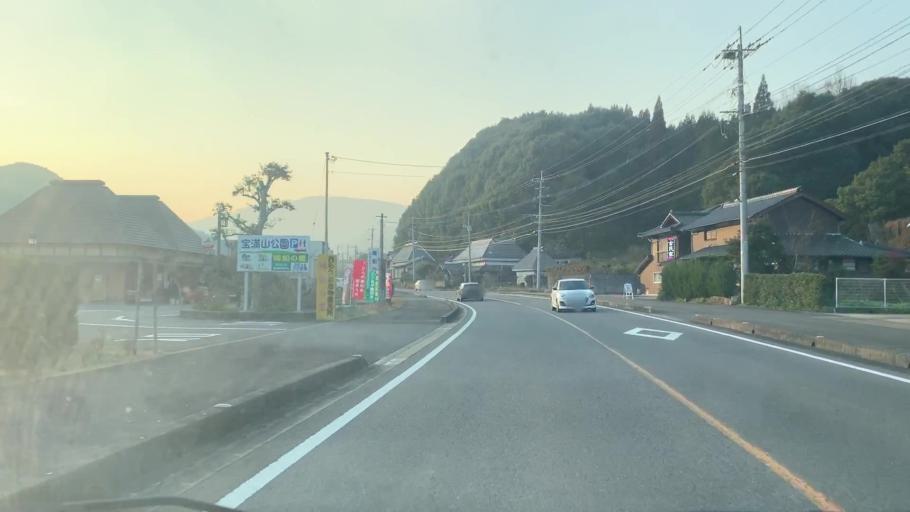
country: JP
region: Saga Prefecture
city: Takeocho-takeo
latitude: 33.2639
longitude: 130.0527
